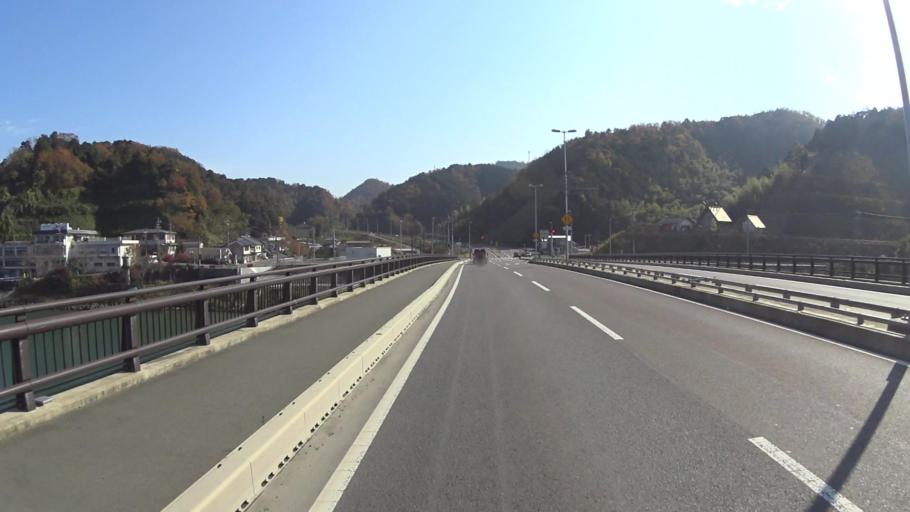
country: JP
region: Kyoto
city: Maizuru
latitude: 35.4515
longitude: 135.2682
